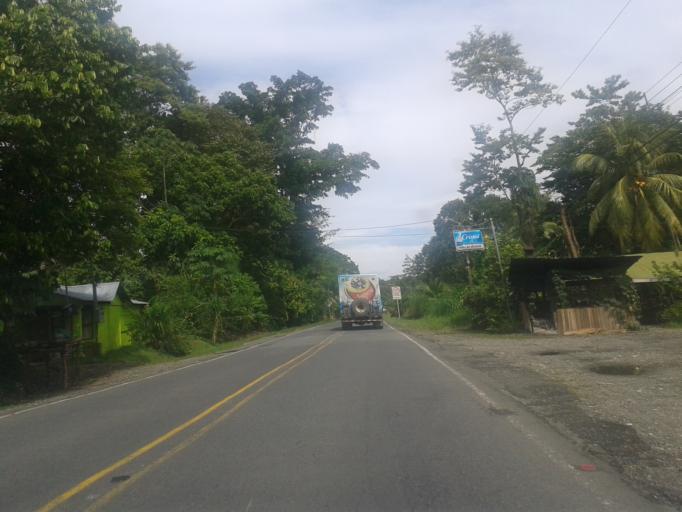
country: CR
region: Limon
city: Limon
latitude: 9.9172
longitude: -83.0097
